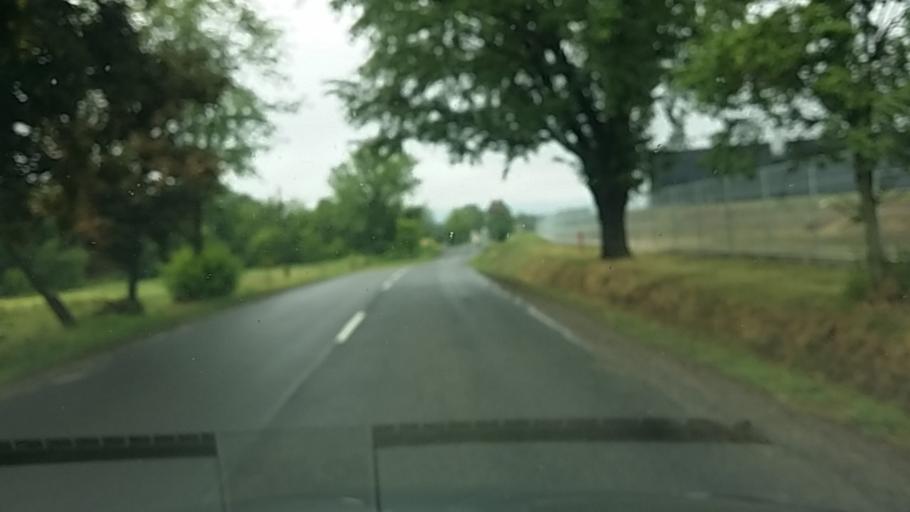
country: HU
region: Komarom-Esztergom
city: Esztergom
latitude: 47.9309
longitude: 18.7768
